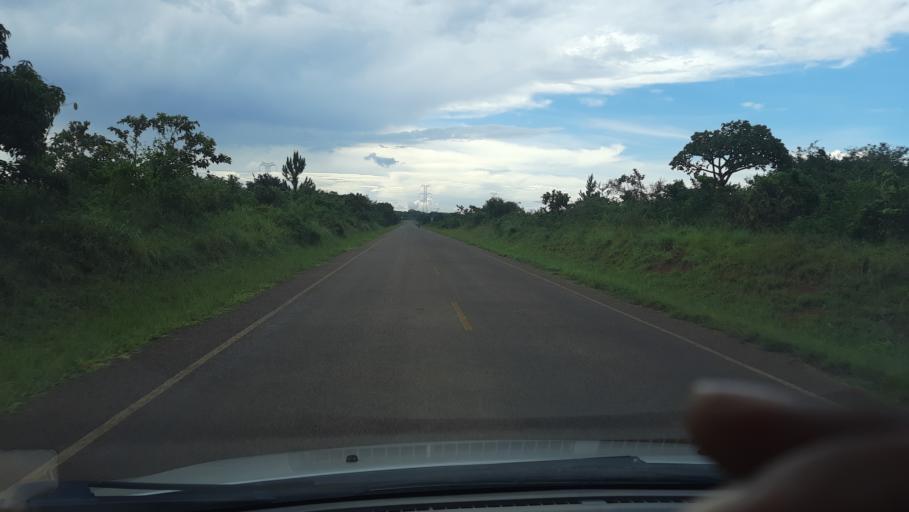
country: UG
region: Central Region
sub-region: Nakasongola District
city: Nakasongola
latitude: 1.3199
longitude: 32.4338
